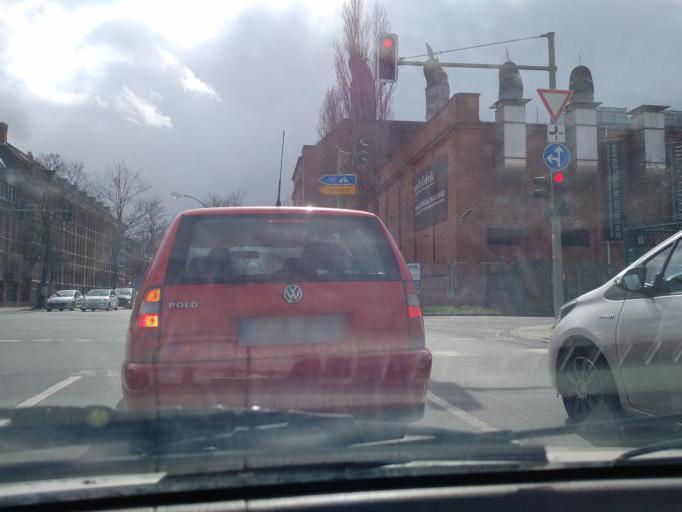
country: DE
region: Berlin
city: Schoneberg Bezirk
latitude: 52.4674
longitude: 13.3671
